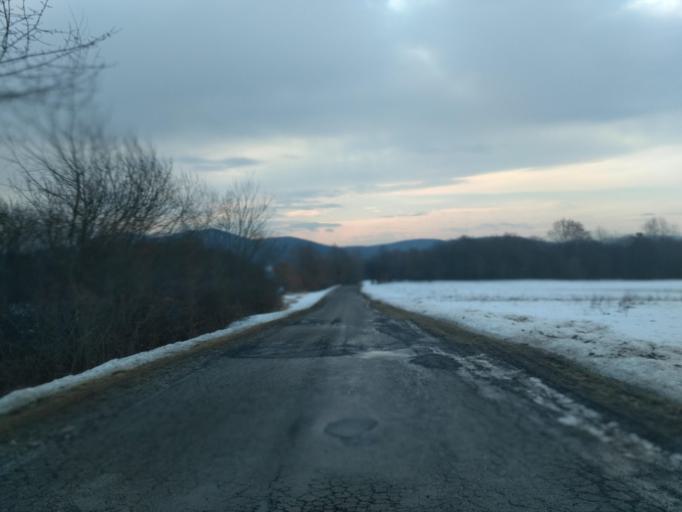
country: PL
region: Subcarpathian Voivodeship
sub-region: Powiat brzozowski
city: Dydnia
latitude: 49.6447
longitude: 22.1604
